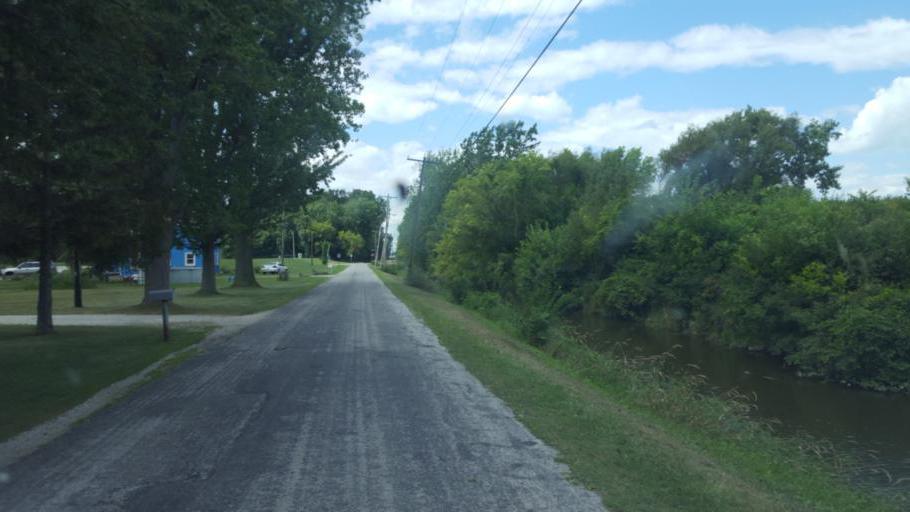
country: US
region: Ohio
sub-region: Lucas County
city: Curtice
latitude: 41.6710
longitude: -83.2769
